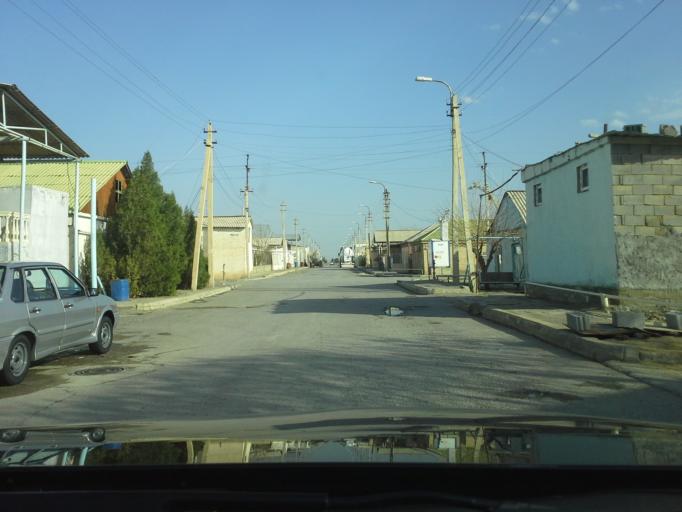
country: TM
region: Ahal
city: Abadan
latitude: 38.0174
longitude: 58.2325
